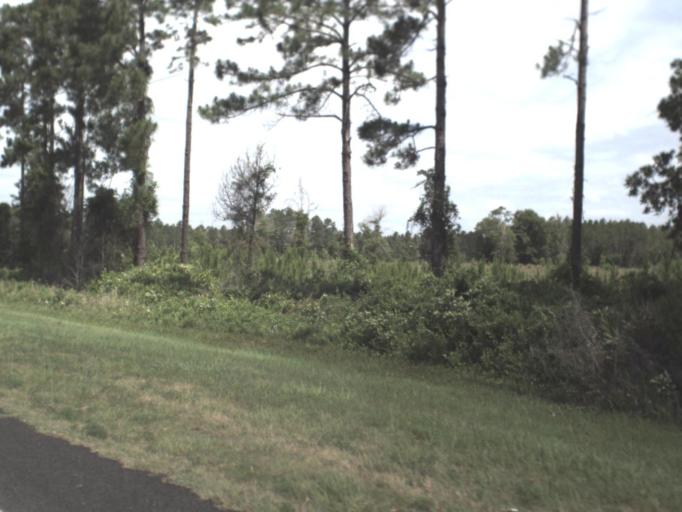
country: US
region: Florida
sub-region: Nassau County
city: Yulee
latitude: 30.6287
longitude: -81.5575
